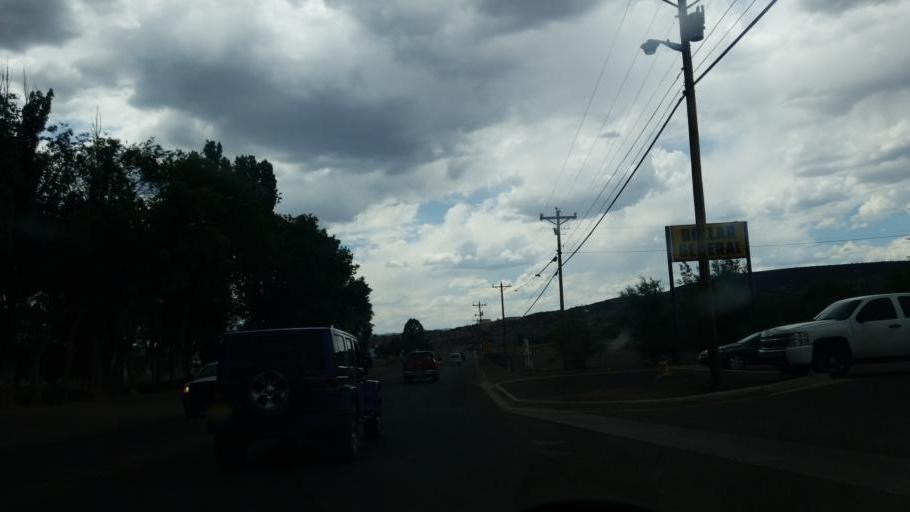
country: US
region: New Mexico
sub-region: Cibola County
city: Grants
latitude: 35.1612
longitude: -107.8358
